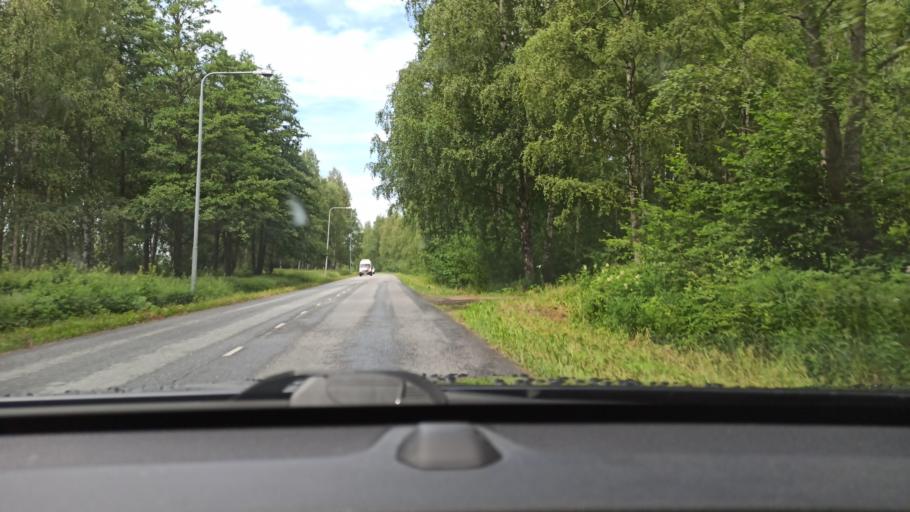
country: FI
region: Satakunta
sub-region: Pori
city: Pori
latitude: 61.5085
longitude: 21.7751
